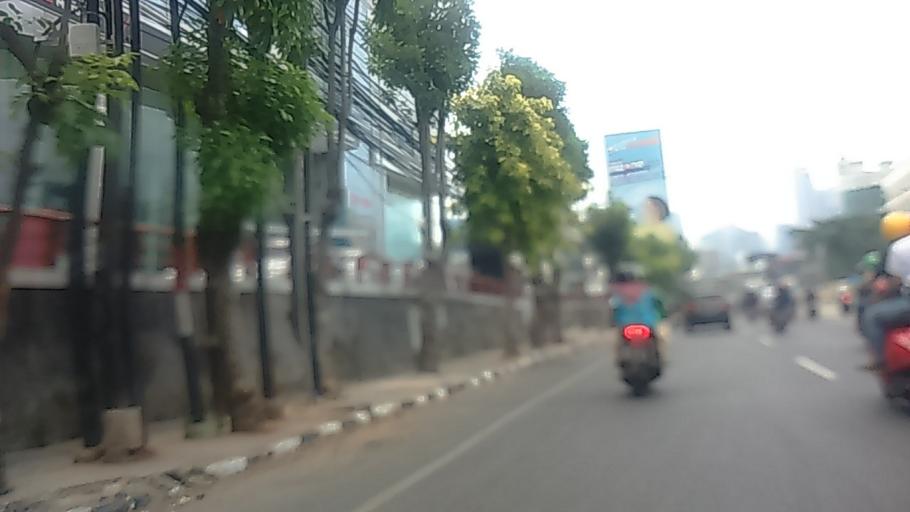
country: ID
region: Jakarta Raya
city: Jakarta
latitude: -6.2445
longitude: 106.8258
